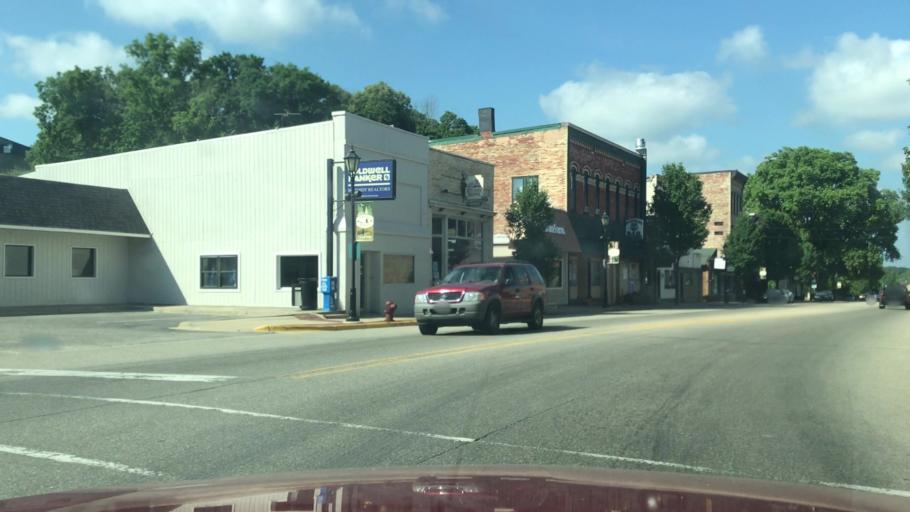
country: US
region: Michigan
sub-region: Newaygo County
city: Newaygo
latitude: 43.4197
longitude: -85.7995
